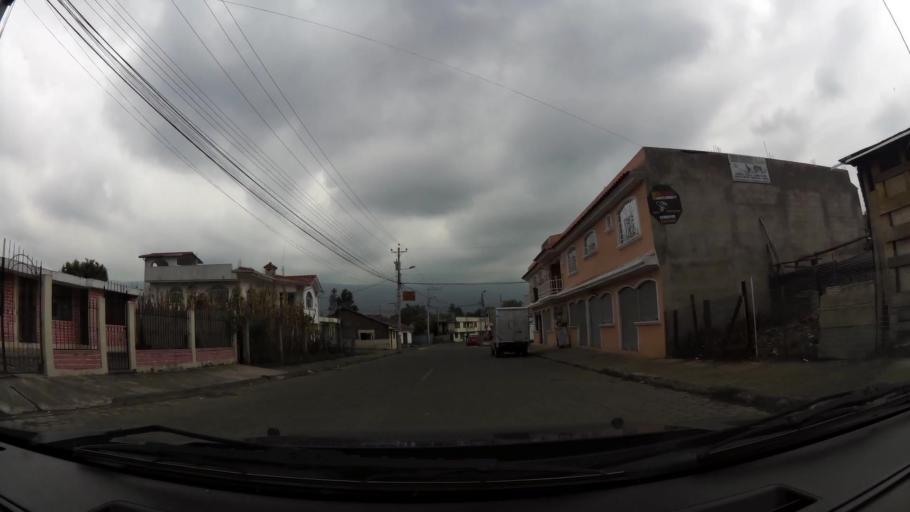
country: EC
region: Pichincha
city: Sangolqui
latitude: -0.3325
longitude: -78.4713
